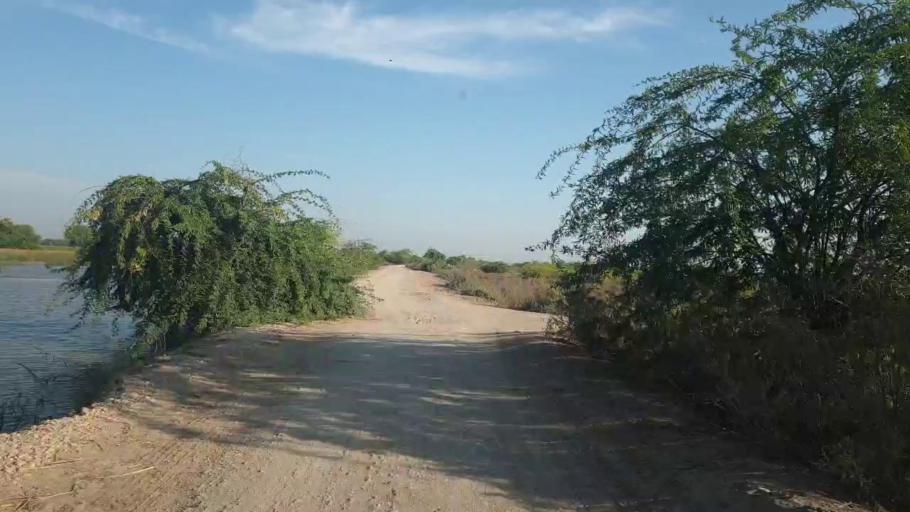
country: PK
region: Sindh
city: Talhar
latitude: 24.8198
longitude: 68.8384
